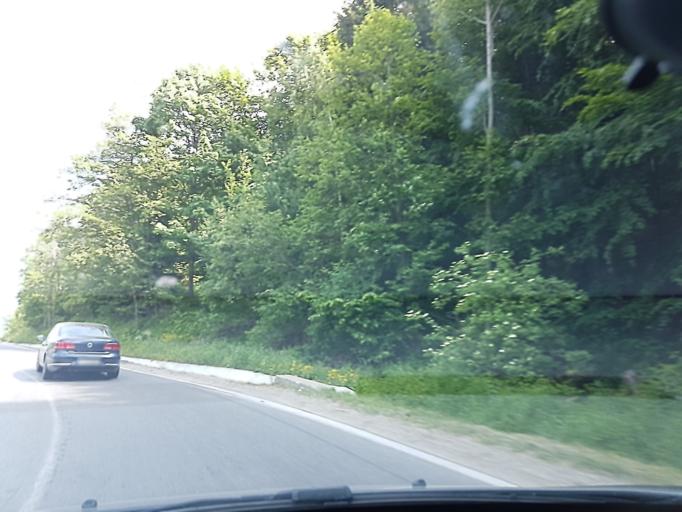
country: RO
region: Prahova
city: Maneciu
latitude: 45.3397
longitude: 25.9567
